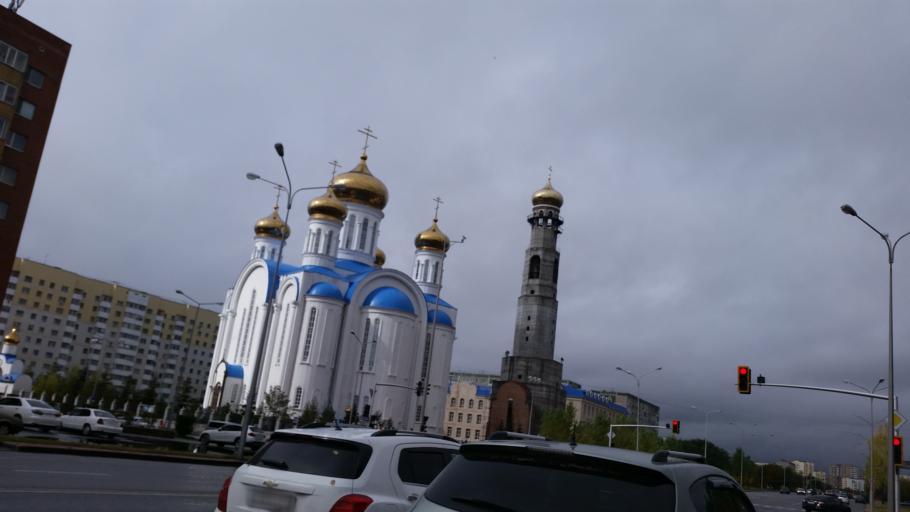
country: KZ
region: Astana Qalasy
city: Astana
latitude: 51.1489
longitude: 71.4833
